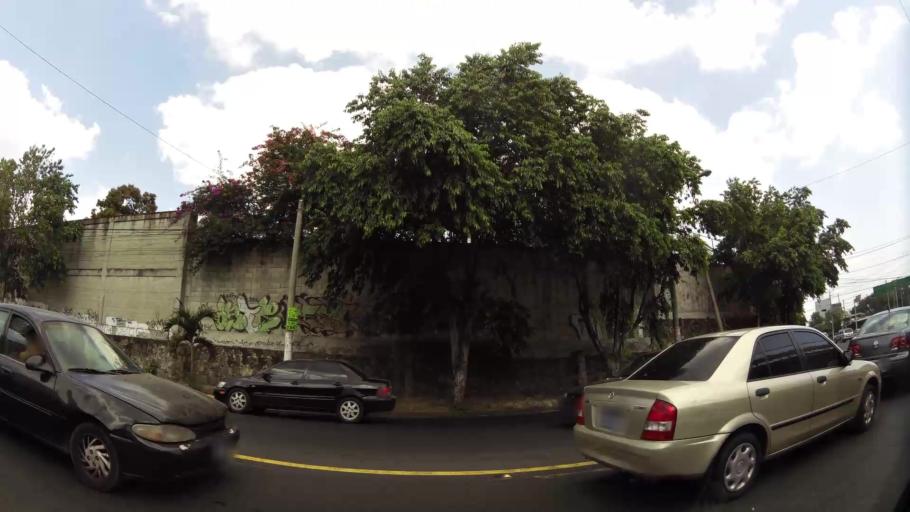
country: SV
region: San Salvador
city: San Salvador
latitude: 13.7040
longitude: -89.2213
